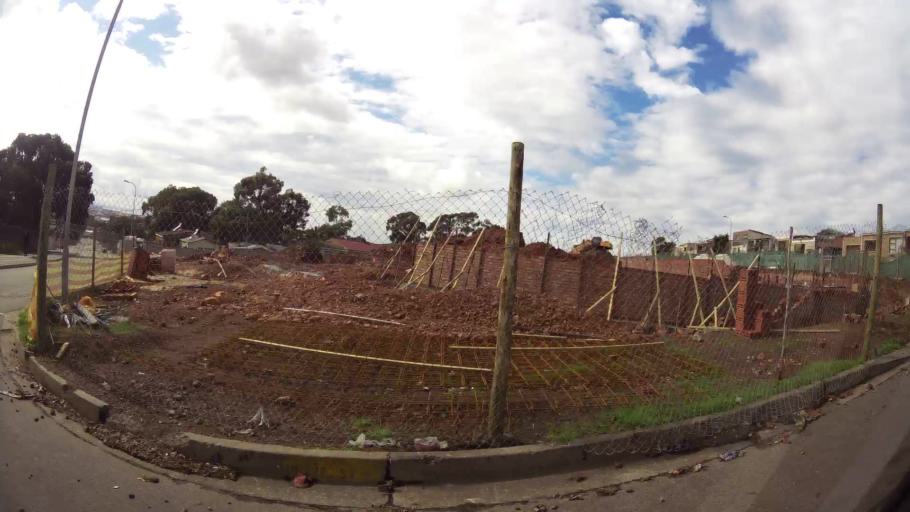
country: ZA
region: Eastern Cape
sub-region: Nelson Mandela Bay Metropolitan Municipality
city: Port Elizabeth
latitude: -33.9309
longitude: 25.5643
